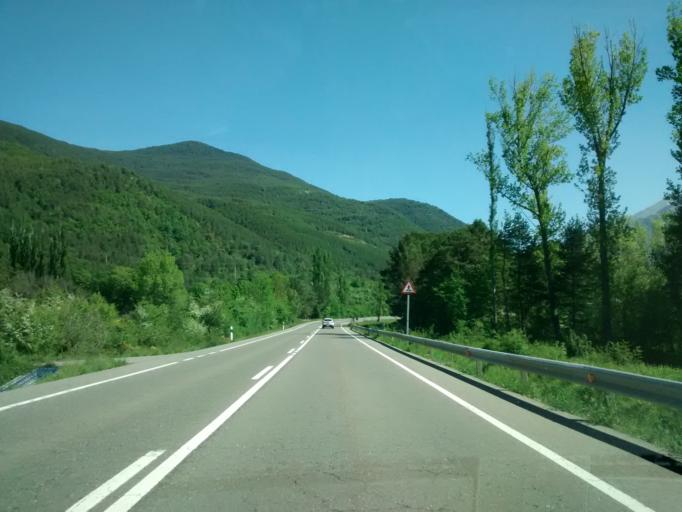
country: ES
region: Aragon
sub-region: Provincia de Huesca
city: Villanua
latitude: 42.6605
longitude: -0.5545
